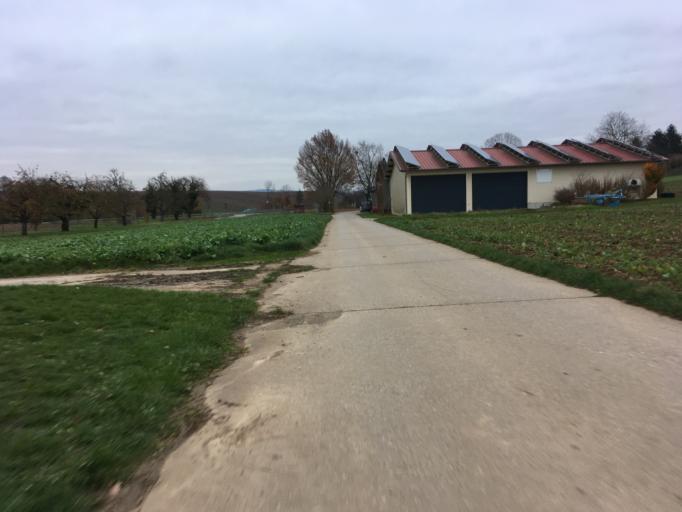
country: DE
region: Baden-Wuerttemberg
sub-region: Regierungsbezirk Stuttgart
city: Nordheim
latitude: 49.0930
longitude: 9.1362
